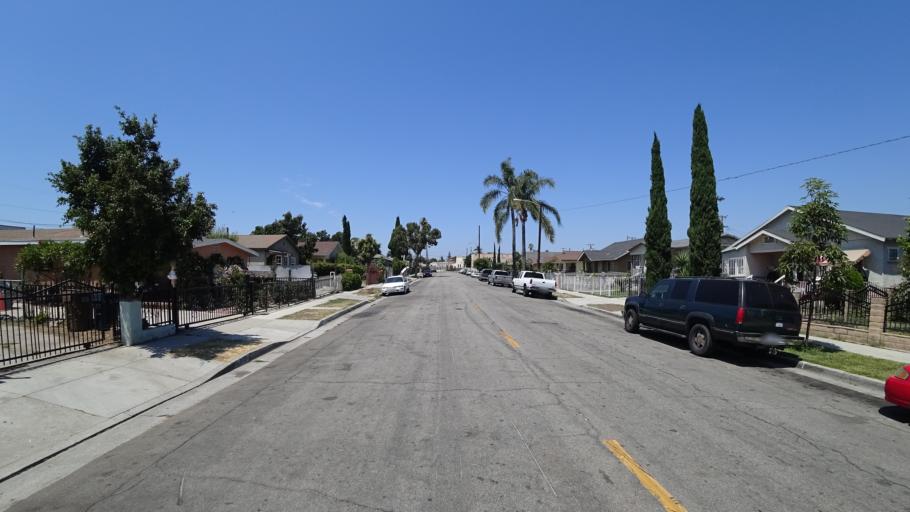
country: US
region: California
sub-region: Los Angeles County
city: Westmont
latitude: 33.9541
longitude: -118.2987
